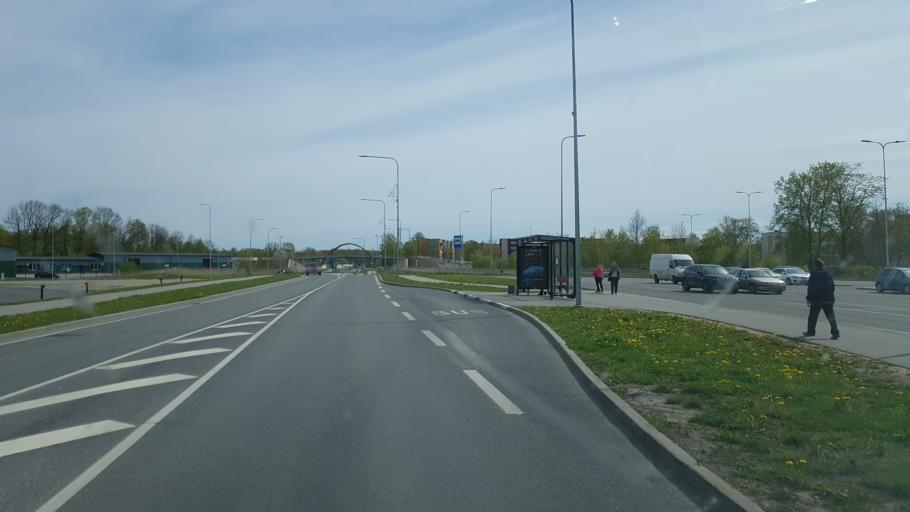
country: EE
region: Ida-Virumaa
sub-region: Johvi vald
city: Johvi
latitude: 59.3524
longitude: 27.4185
